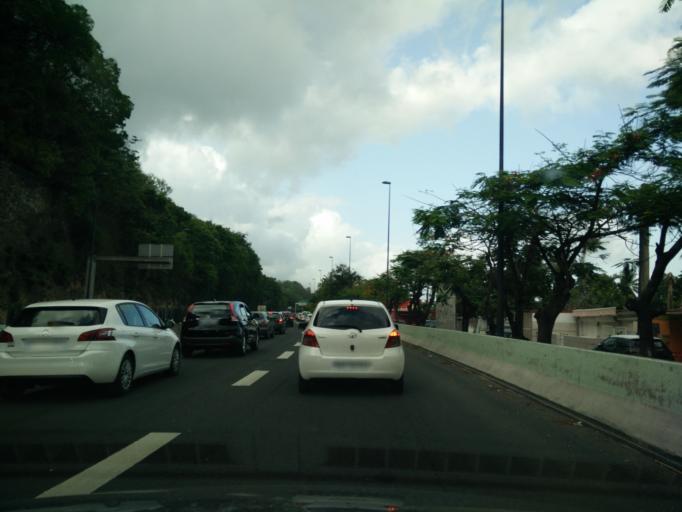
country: GP
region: Guadeloupe
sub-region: Guadeloupe
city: Le Gosier
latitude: 16.2179
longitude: -61.5102
